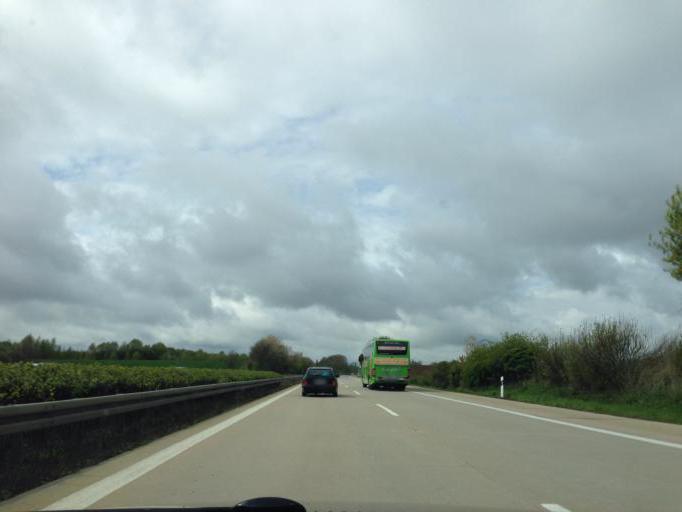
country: DE
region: Saxony
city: Dobeln
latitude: 51.1570
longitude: 13.1181
